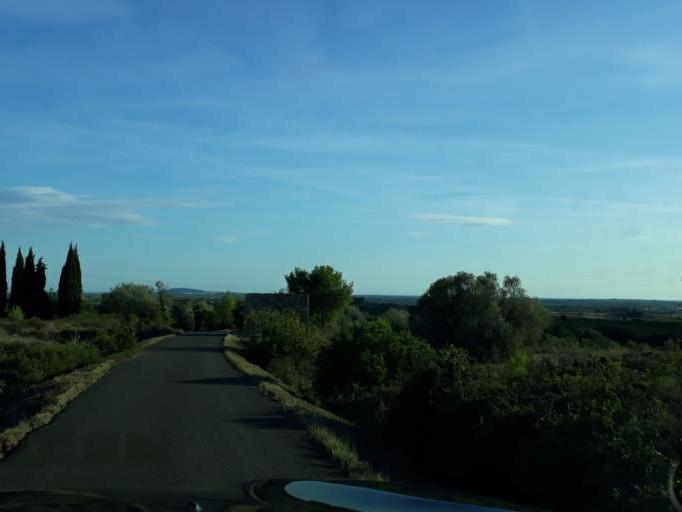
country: FR
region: Languedoc-Roussillon
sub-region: Departement de l'Herault
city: Florensac
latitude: 43.4186
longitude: 3.4738
